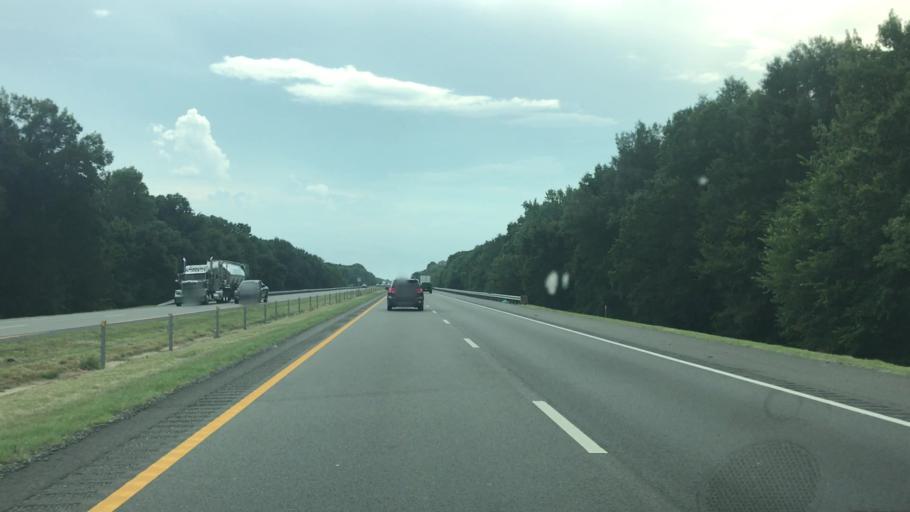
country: US
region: Arkansas
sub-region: Monroe County
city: Brinkley
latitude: 34.8941
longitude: -91.2477
